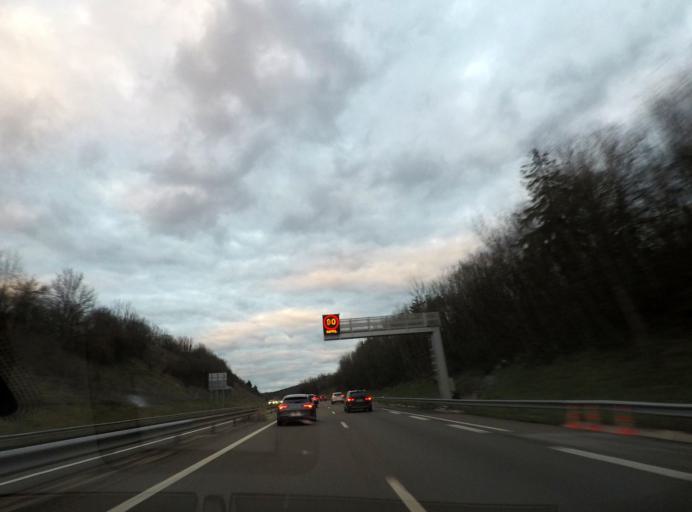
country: FR
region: Rhone-Alpes
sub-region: Departement de l'Ain
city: Saint-Martin-du-Frene
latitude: 46.1218
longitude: 5.4960
